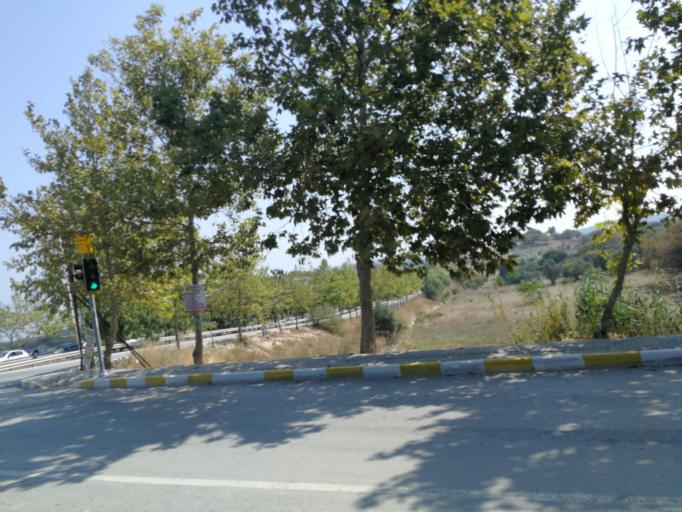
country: TR
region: Izmir
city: Urla
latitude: 38.3264
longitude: 26.7724
